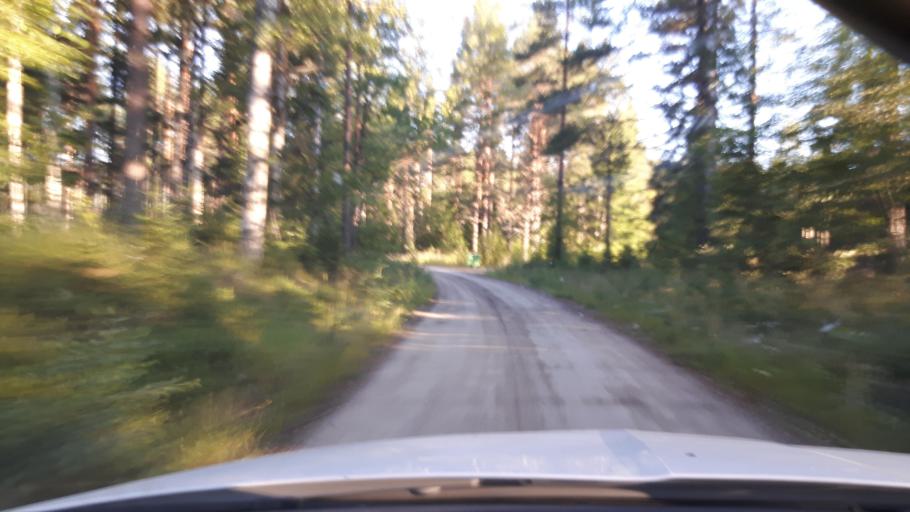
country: SE
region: Gaevleborg
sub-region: Ljusdals Kommun
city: Farila
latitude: 62.0441
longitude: 15.8271
